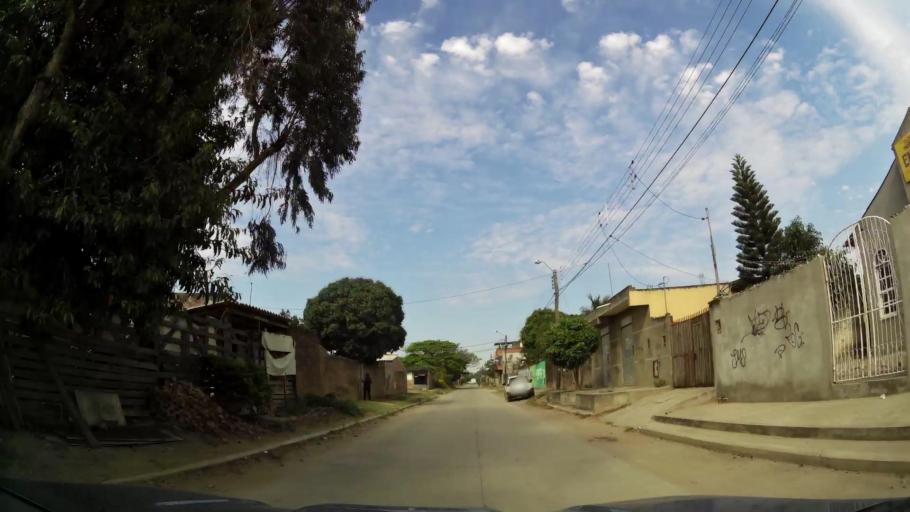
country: BO
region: Santa Cruz
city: Santa Cruz de la Sierra
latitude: -17.7337
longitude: -63.1368
